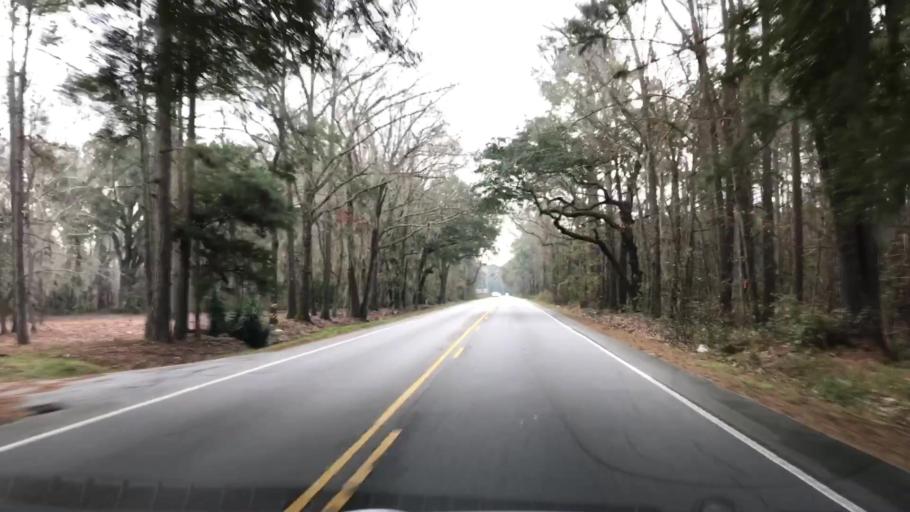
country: US
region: South Carolina
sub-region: Jasper County
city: Ridgeland
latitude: 32.5675
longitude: -80.9176
